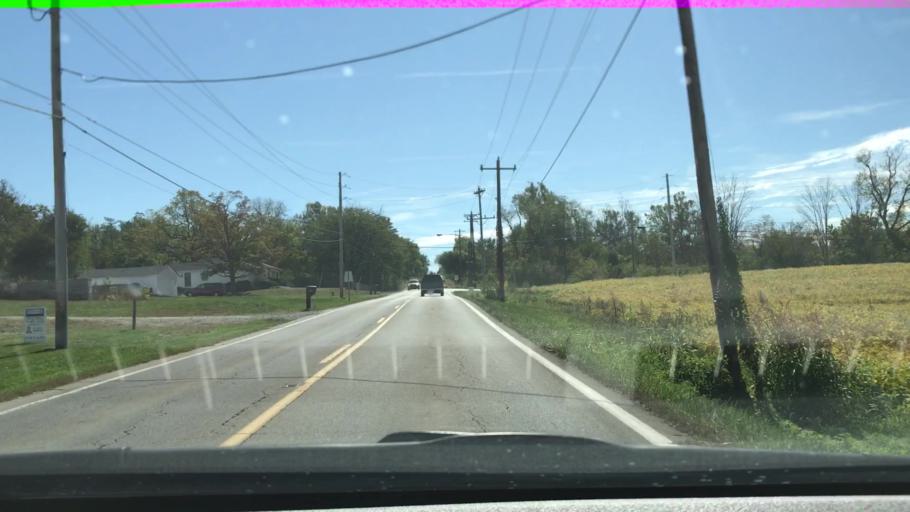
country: US
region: Ohio
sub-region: Butler County
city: Hamilton
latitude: 39.4543
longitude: -84.6237
